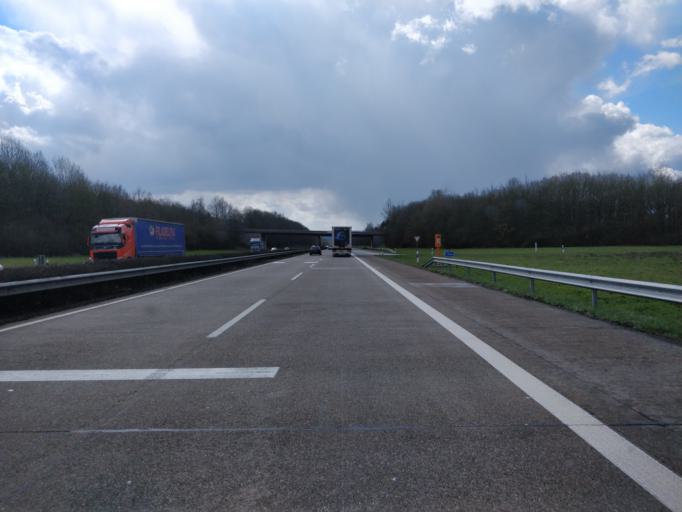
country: DE
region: Rheinland-Pfalz
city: Esch
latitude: 49.9031
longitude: 6.8532
